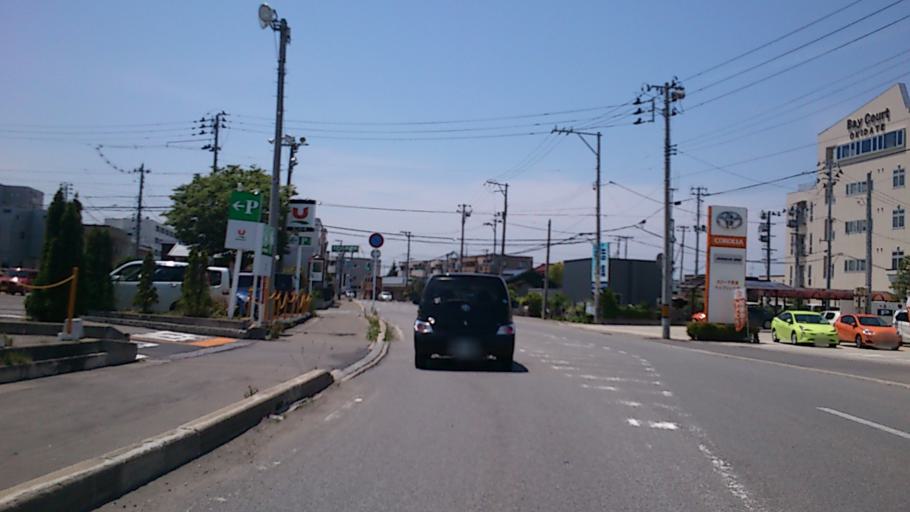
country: JP
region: Aomori
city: Aomori Shi
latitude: 40.8355
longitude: 140.7259
